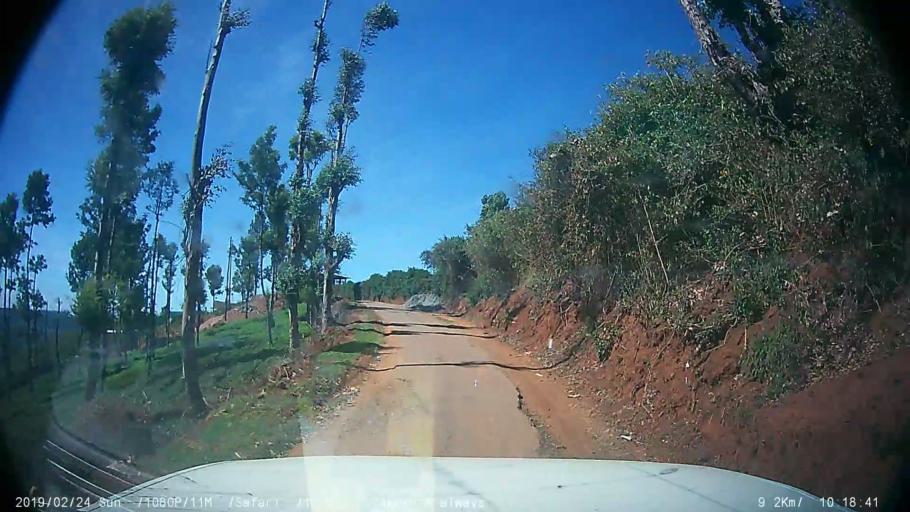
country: IN
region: Tamil Nadu
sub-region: Nilgiri
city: Ooty
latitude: 11.3869
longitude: 76.7205
